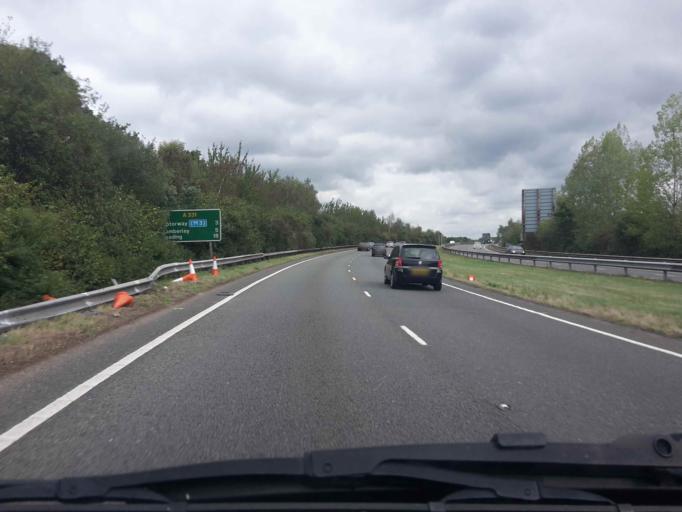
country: GB
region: England
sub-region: Hampshire
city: Farnborough
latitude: 51.2783
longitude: -0.7350
